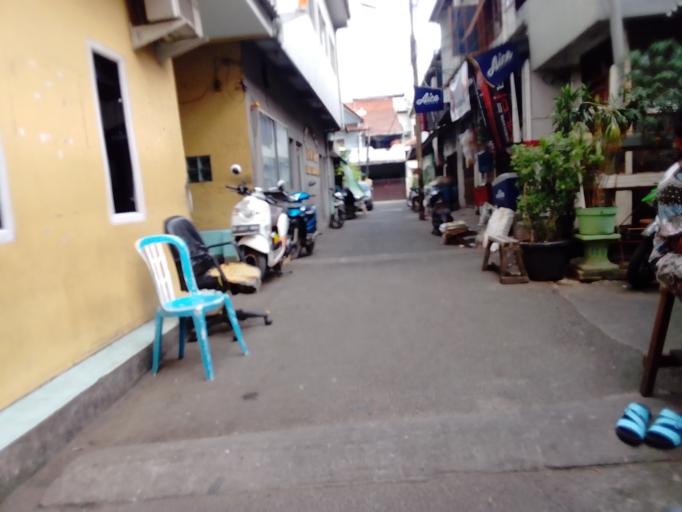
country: ID
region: Jakarta Raya
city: Jakarta
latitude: -6.1519
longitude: 106.8157
